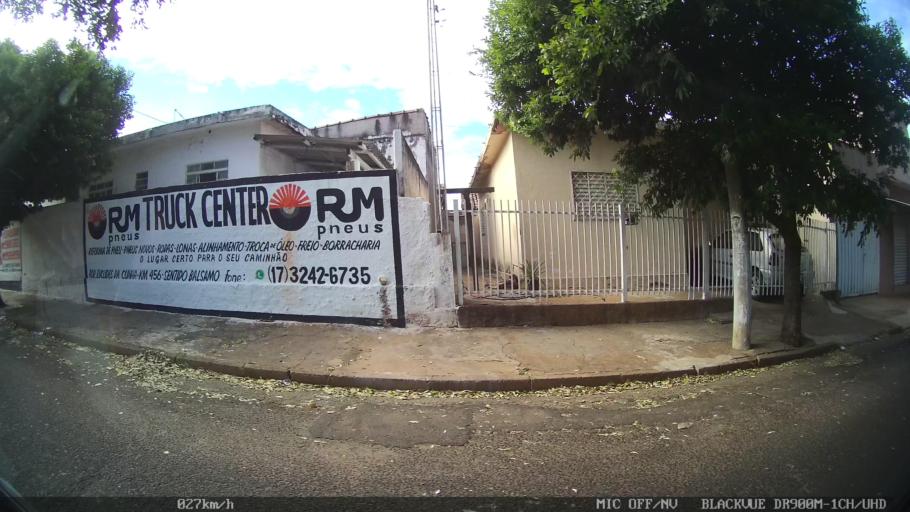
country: BR
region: Sao Paulo
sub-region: Bady Bassitt
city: Bady Bassitt
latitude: -20.8227
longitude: -49.5232
